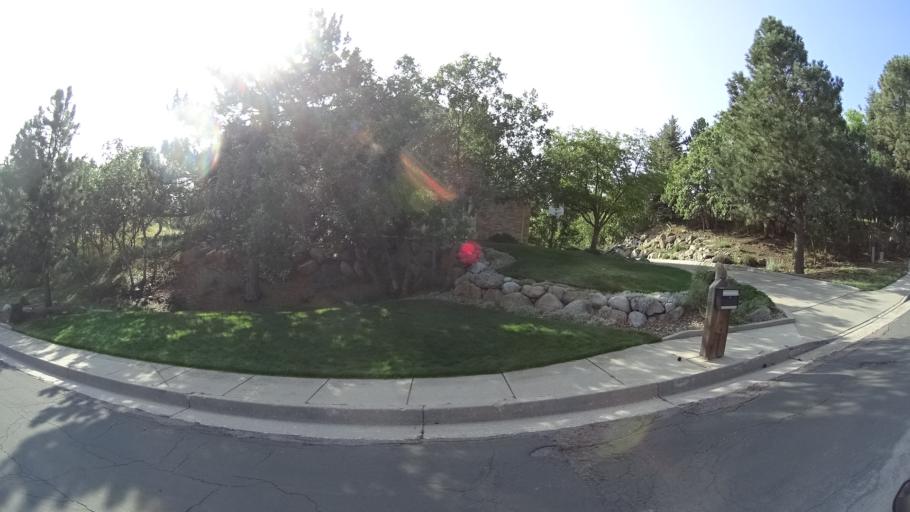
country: US
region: Colorado
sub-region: El Paso County
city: Manitou Springs
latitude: 38.8230
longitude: -104.8762
